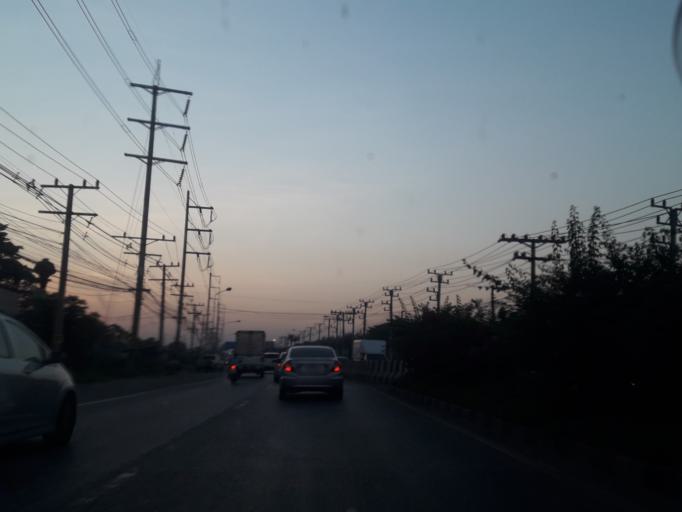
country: TH
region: Pathum Thani
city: Thanyaburi
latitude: 14.0670
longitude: 100.7030
